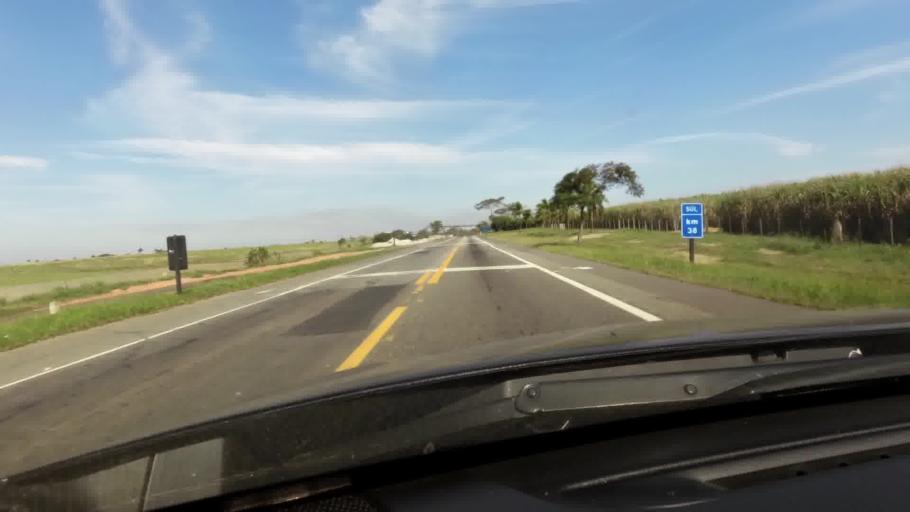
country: BR
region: Rio de Janeiro
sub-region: Campos Dos Goytacazes
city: Campos
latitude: -21.5332
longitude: -41.3404
